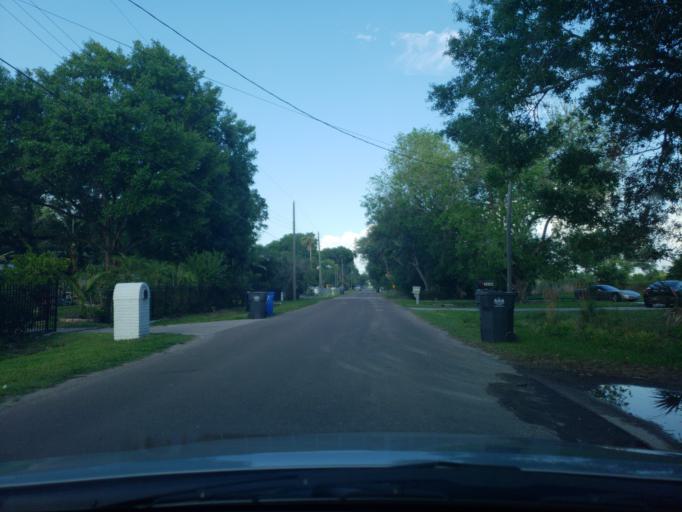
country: US
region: Florida
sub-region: Hillsborough County
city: Palm River-Clair Mel
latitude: 27.9155
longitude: -82.3886
